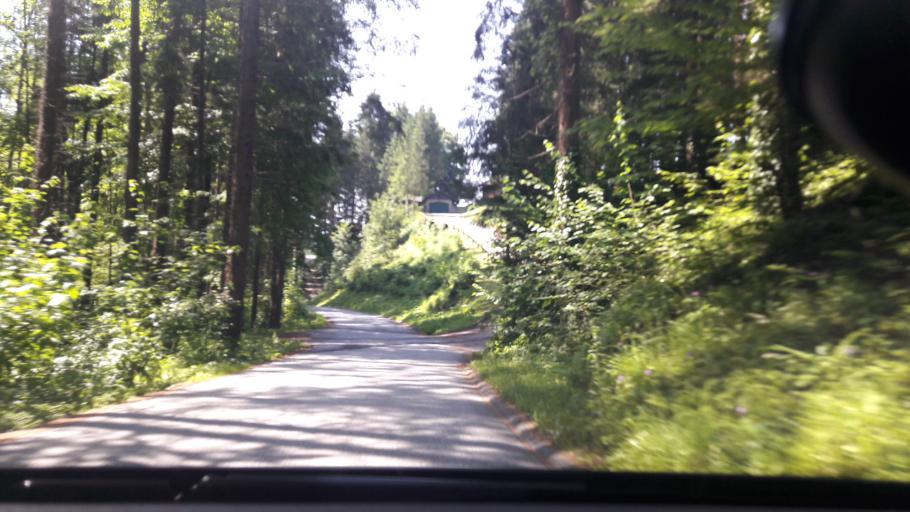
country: AT
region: Styria
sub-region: Politischer Bezirk Graz-Umgebung
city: Stiwoll
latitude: 47.1062
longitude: 15.1926
